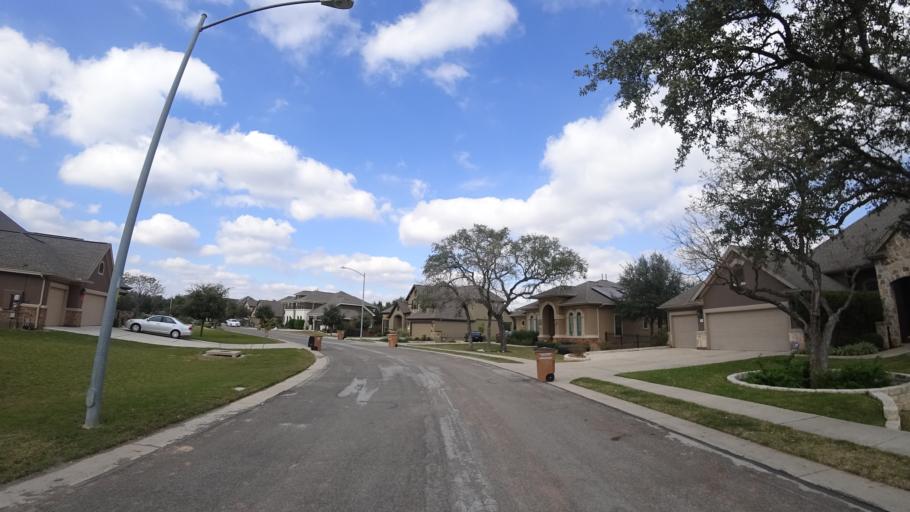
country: US
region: Texas
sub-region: Travis County
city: Shady Hollow
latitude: 30.1743
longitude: -97.8482
